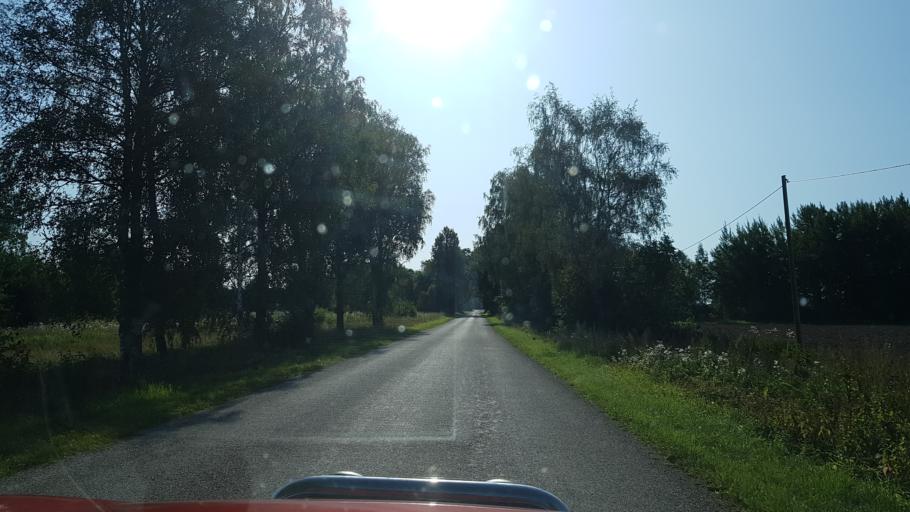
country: LV
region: Apes Novads
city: Ape
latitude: 57.6626
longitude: 26.6921
